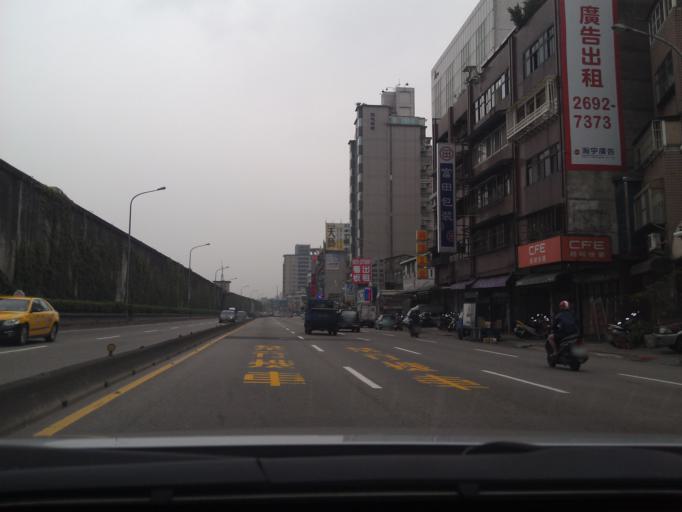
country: TW
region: Taipei
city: Taipei
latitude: 25.0657
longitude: 121.5089
